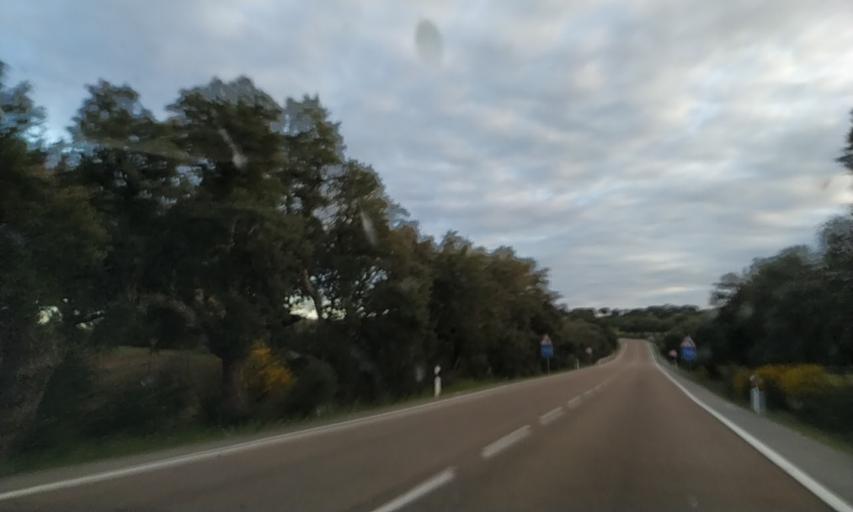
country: ES
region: Extremadura
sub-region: Provincia de Badajoz
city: Puebla de Obando
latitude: 39.2498
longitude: -6.5571
